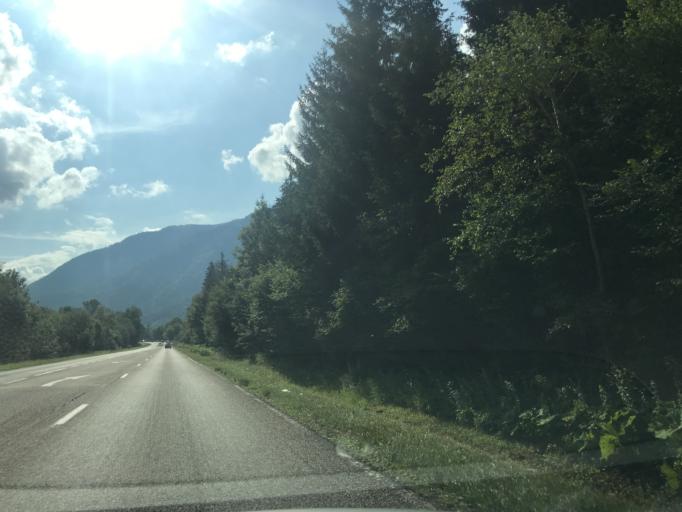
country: FR
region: Rhone-Alpes
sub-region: Departement de la Haute-Savoie
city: Dingy-Saint-Clair
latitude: 45.8954
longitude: 6.2331
